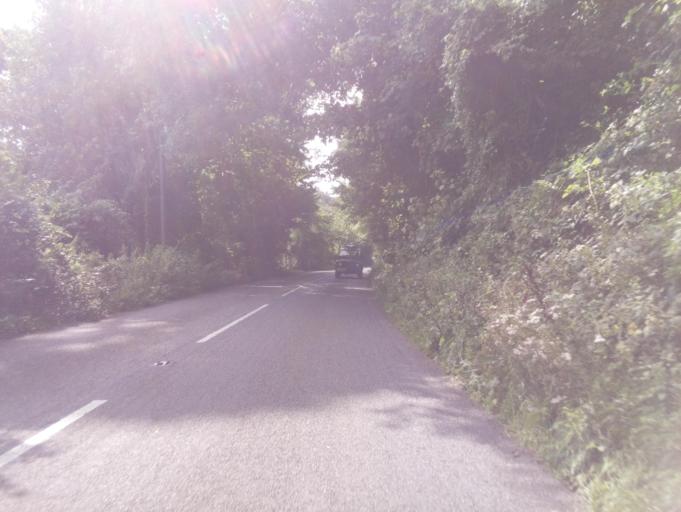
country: GB
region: England
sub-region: Devon
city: Dartmouth
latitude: 50.3596
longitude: -3.5613
